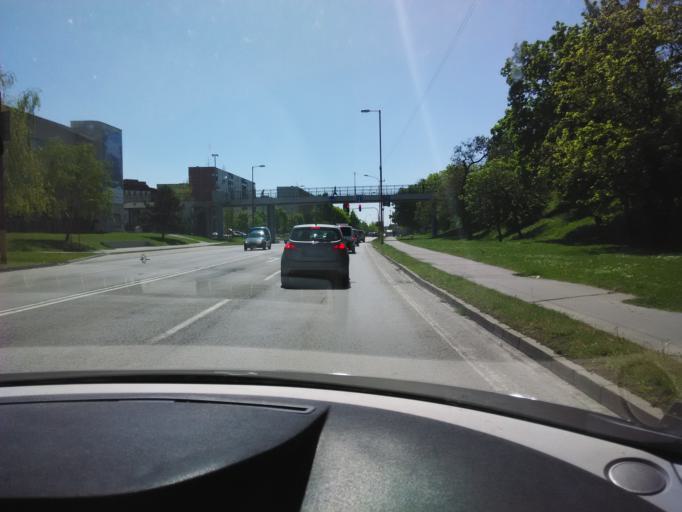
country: SK
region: Trnavsky
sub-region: Okres Trnava
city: Trnava
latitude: 48.3801
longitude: 17.5926
